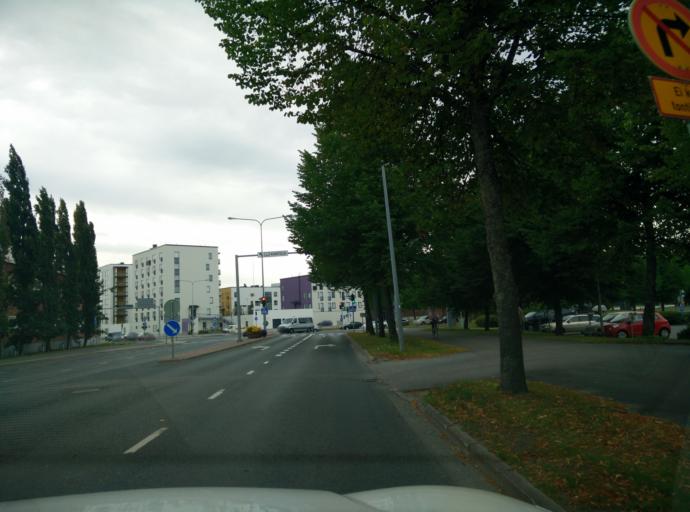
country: FI
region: Haeme
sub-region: Haemeenlinna
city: Haemeenlinna
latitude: 60.9976
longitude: 24.4787
